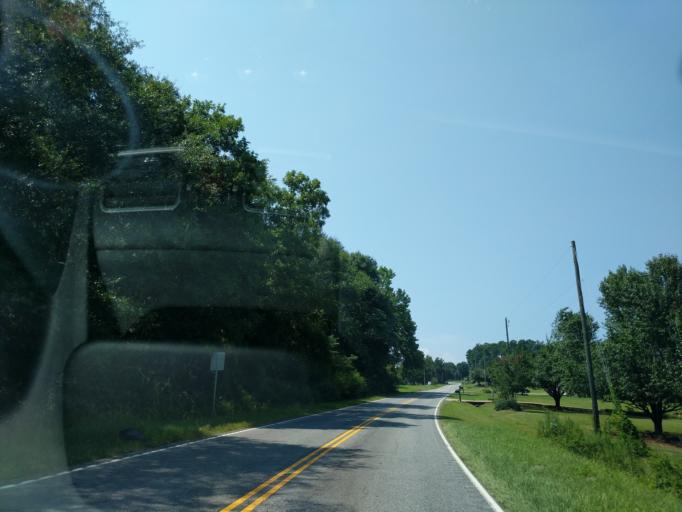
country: US
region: South Carolina
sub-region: Greenville County
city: Greer
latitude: 34.9658
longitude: -82.1933
